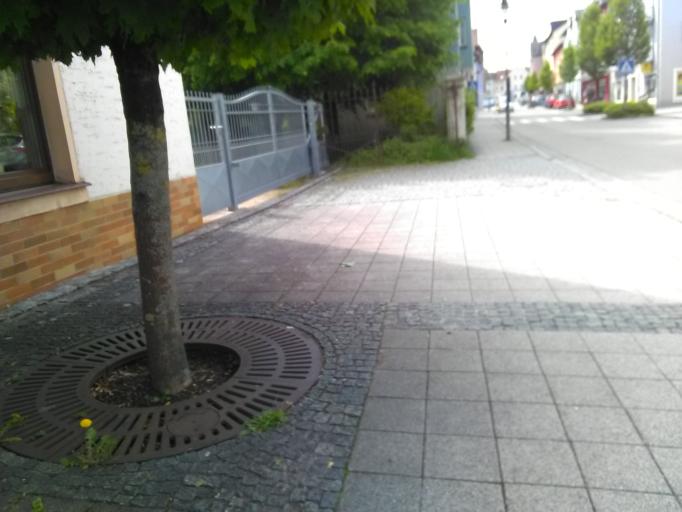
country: DE
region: Bavaria
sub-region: Regierungsbezirk Mittelfranken
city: Treuchtlingen
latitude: 48.9571
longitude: 10.9088
